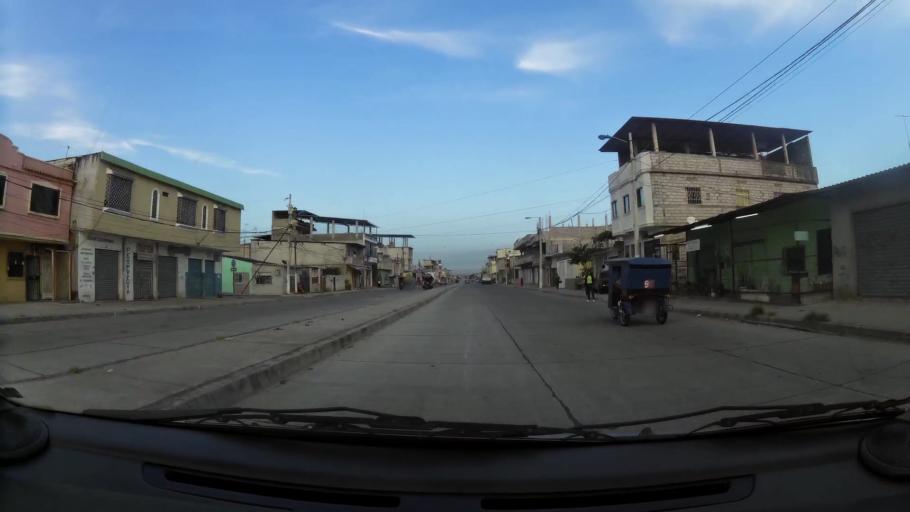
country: EC
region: Guayas
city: Eloy Alfaro
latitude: -2.0879
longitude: -79.9025
